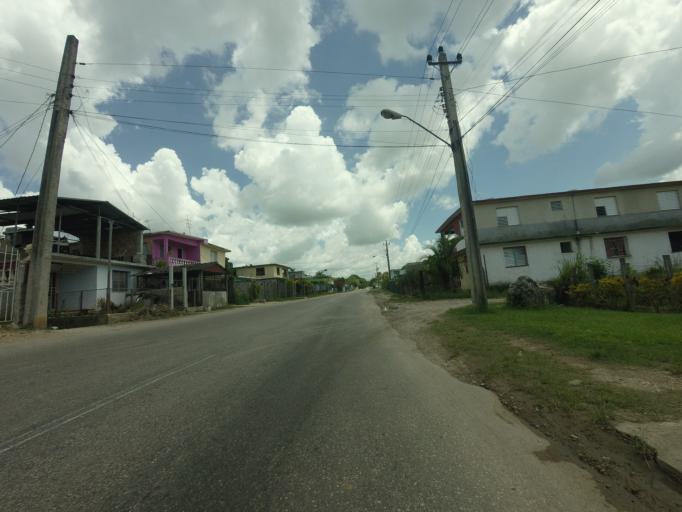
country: CU
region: La Habana
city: Arroyo Naranjo
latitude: 23.0142
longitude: -82.3019
